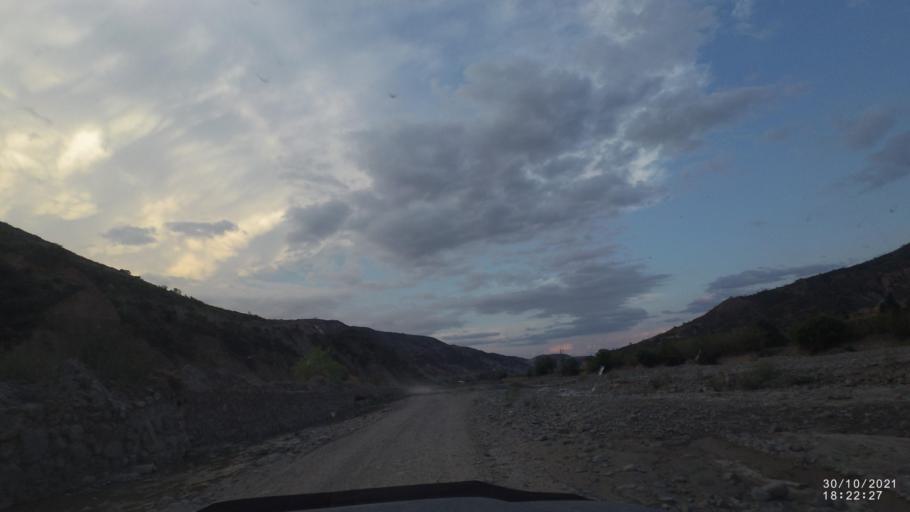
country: BO
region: Cochabamba
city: Sipe Sipe
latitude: -17.5472
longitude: -66.4066
